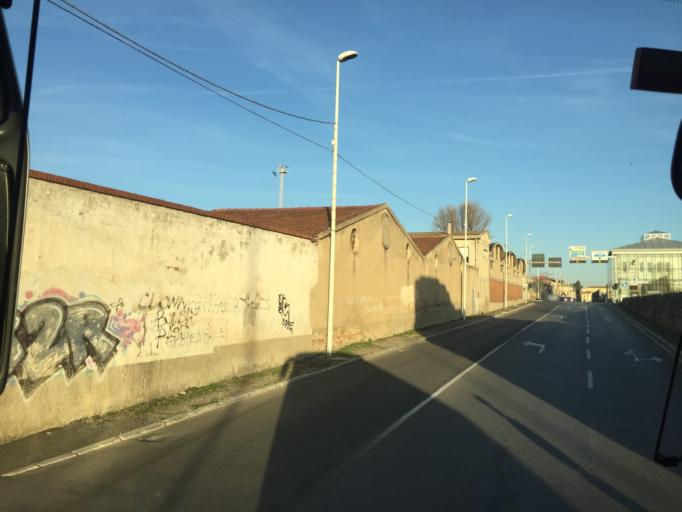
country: IT
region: Tuscany
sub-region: Provincia di Livorno
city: Livorno
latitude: 43.5590
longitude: 10.3085
